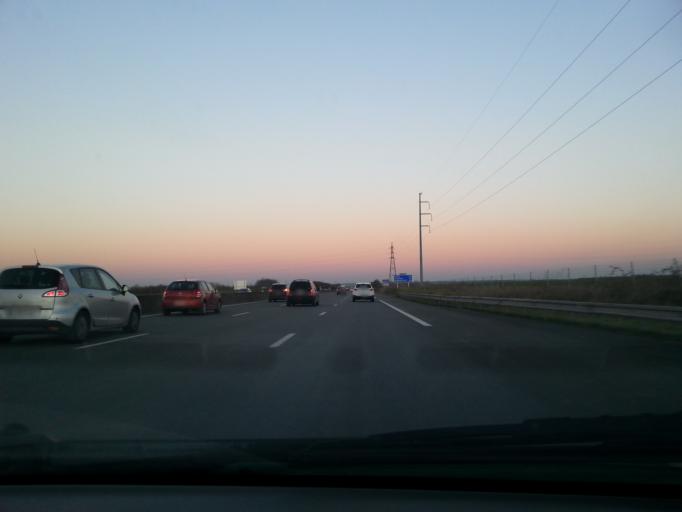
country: FR
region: Centre
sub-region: Departement d'Eure-et-Loir
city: Dammarie
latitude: 48.3691
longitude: 1.4589
